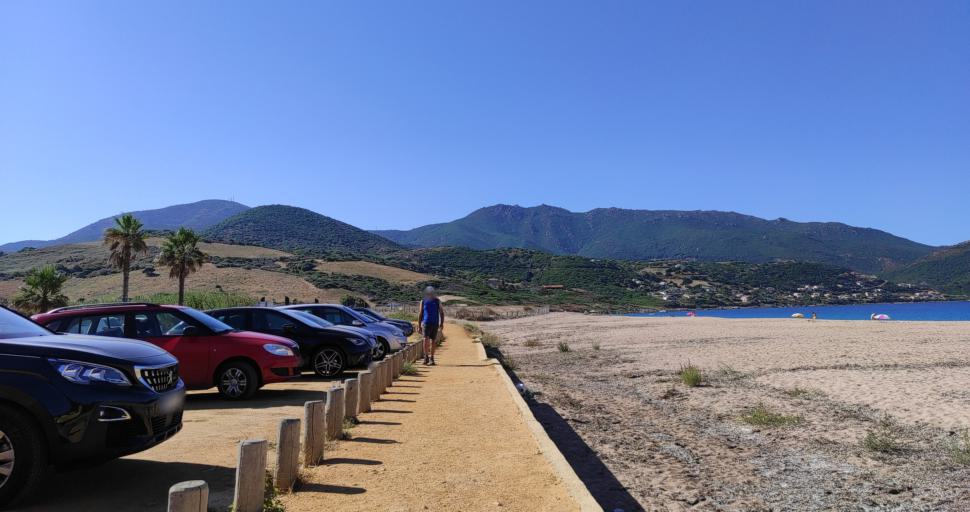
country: FR
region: Corsica
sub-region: Departement de la Corse-du-Sud
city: Alata
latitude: 41.9914
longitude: 8.6696
